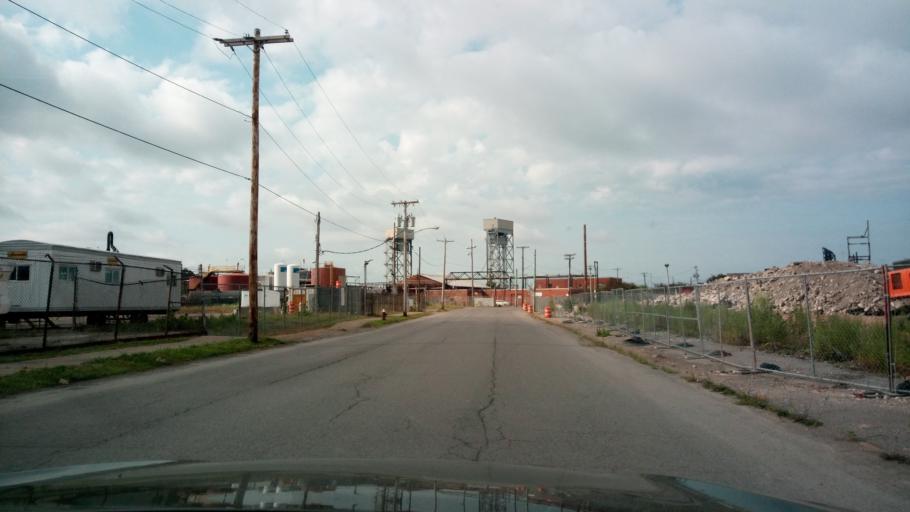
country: US
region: New York
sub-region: Erie County
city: Buffalo
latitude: 42.8666
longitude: -78.8419
